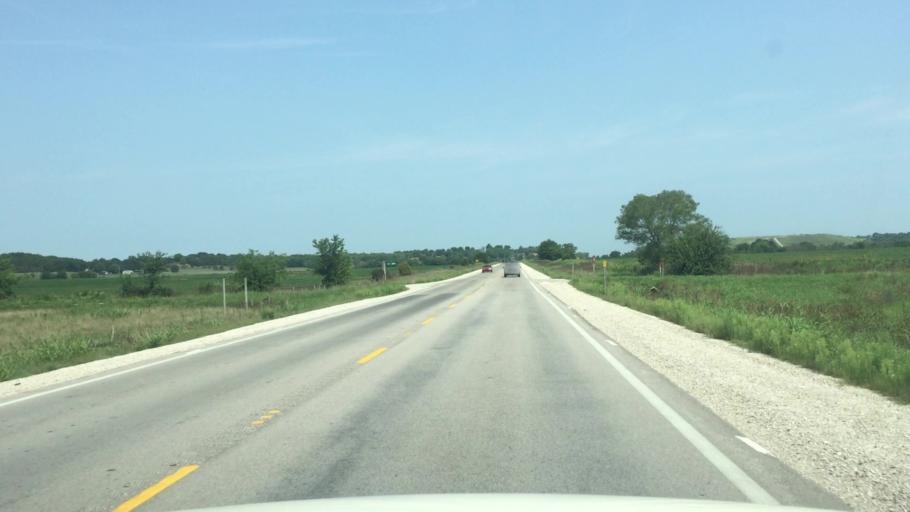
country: US
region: Kansas
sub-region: Montgomery County
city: Cherryvale
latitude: 37.1938
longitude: -95.5813
